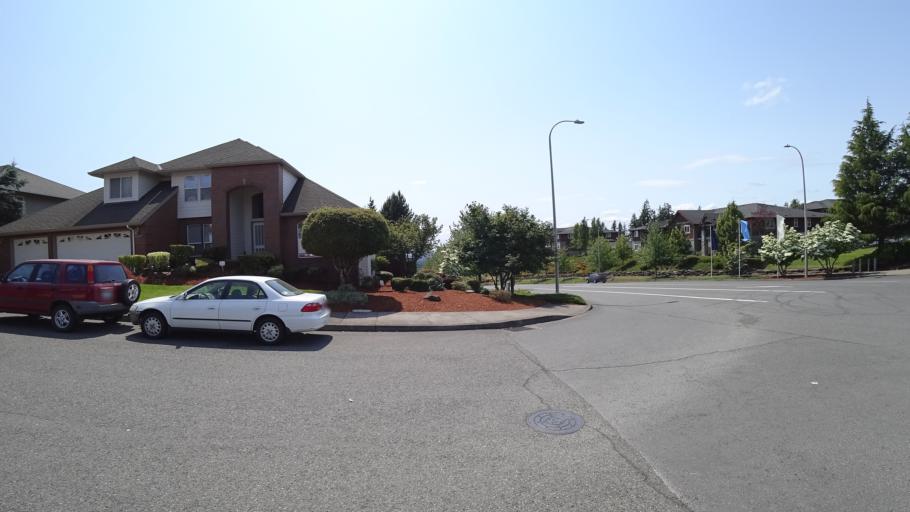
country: US
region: Oregon
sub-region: Multnomah County
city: Lents
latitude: 45.4563
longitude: -122.5616
